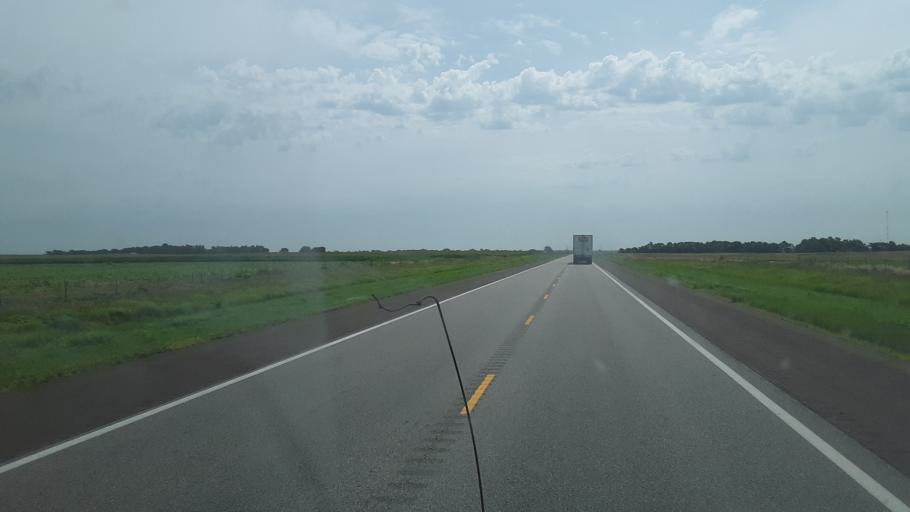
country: US
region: Kansas
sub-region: Reno County
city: Nickerson
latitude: 37.9852
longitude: -98.0988
